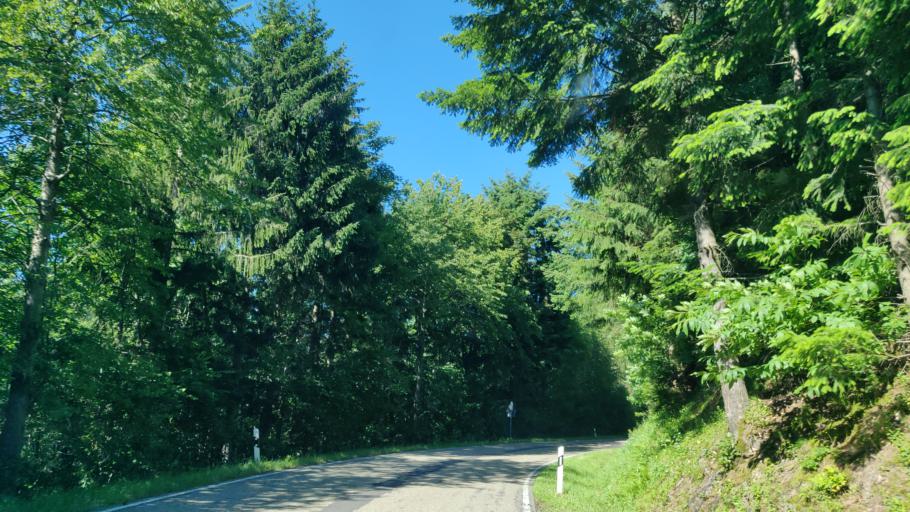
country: DE
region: Baden-Wuerttemberg
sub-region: Karlsruhe Region
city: Gernsbach
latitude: 48.7479
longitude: 8.3114
